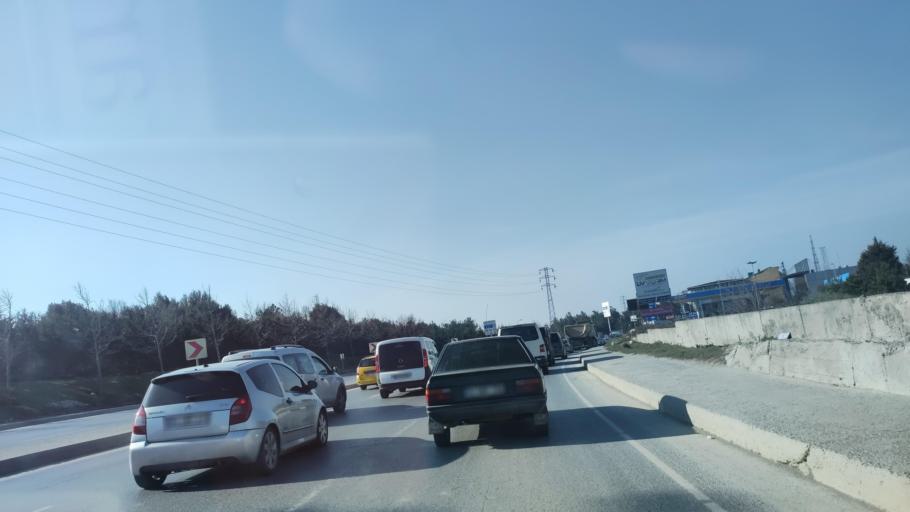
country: TR
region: Istanbul
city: Basaksehir
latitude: 41.1501
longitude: 28.7883
